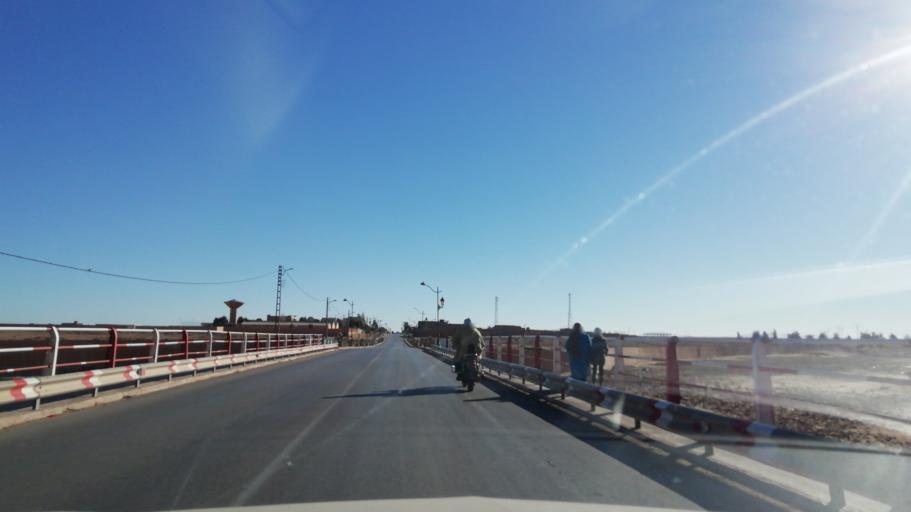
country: DZ
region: El Bayadh
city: El Bayadh
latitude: 33.8528
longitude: 0.6370
